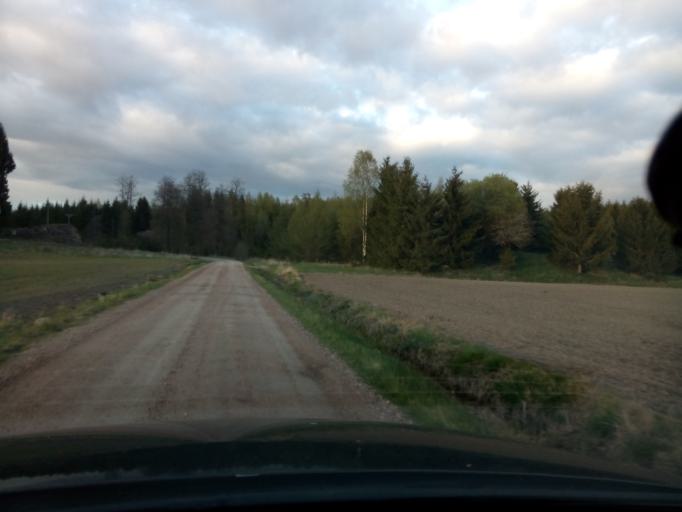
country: SE
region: Soedermanland
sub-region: Oxelosunds Kommun
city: Oxelosund
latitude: 58.7790
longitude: 17.2683
